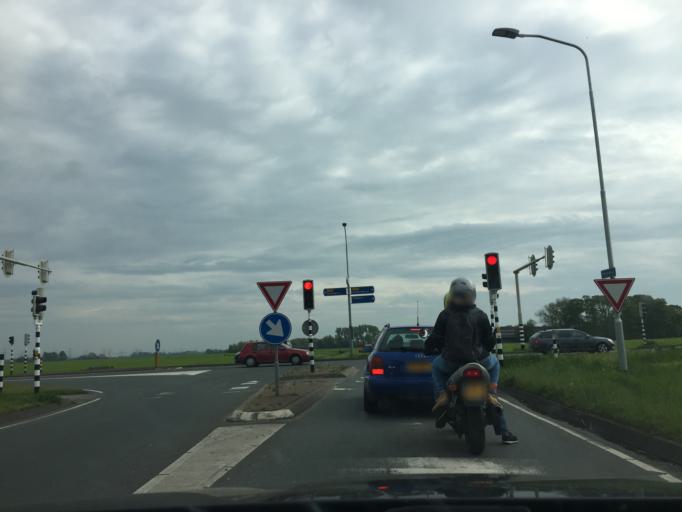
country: NL
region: Groningen
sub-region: Gemeente Zuidhorn
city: Aduard
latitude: 53.2494
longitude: 6.4584
